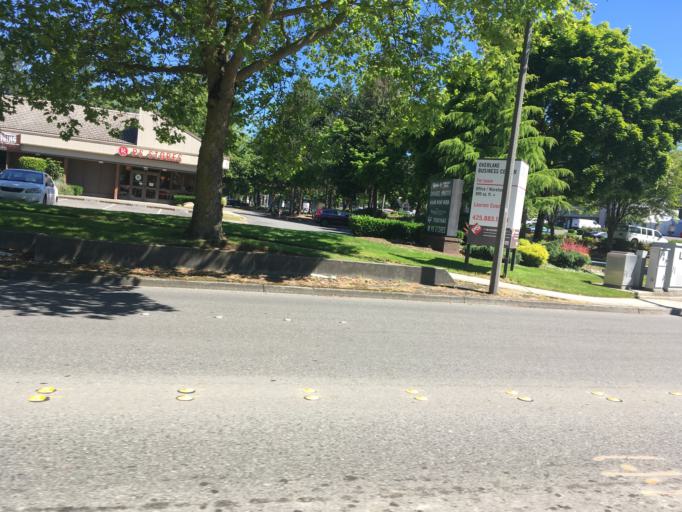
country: US
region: Washington
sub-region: King County
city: Redmond
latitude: 47.6315
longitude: -122.1383
